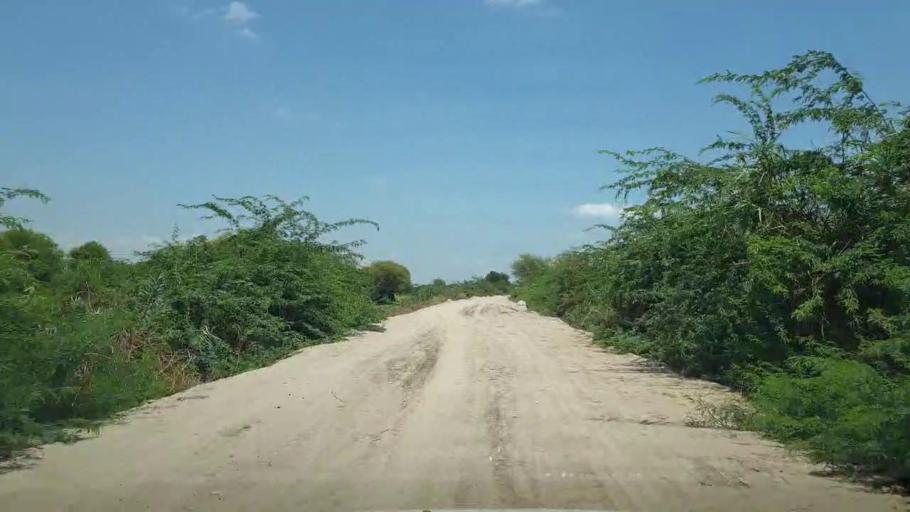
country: PK
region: Sindh
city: Sanghar
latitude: 26.1071
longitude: 69.0090
